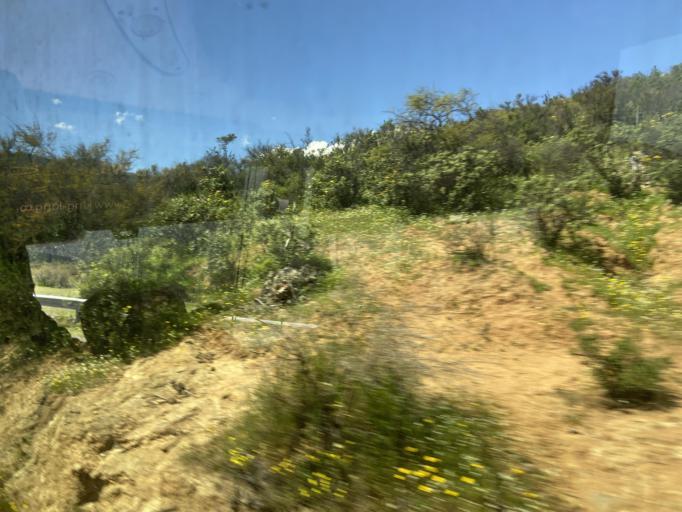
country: CL
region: Valparaiso
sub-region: Provincia de Marga Marga
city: Villa Alemana
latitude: -33.1893
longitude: -71.2927
